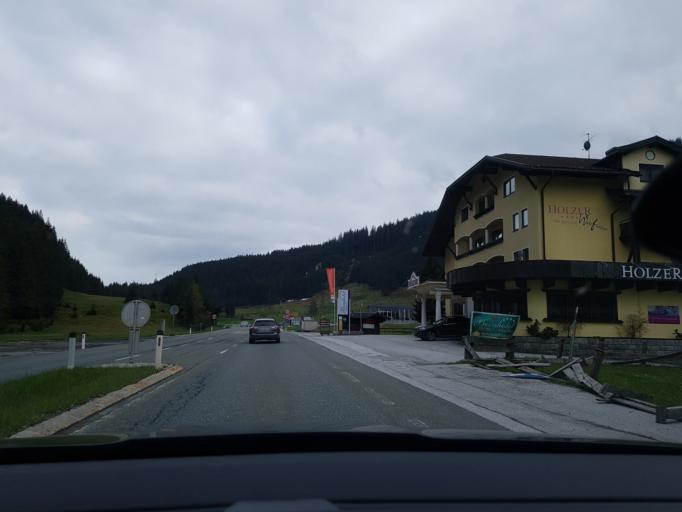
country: AT
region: Salzburg
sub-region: Politischer Bezirk Zell am See
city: Hollersbach im Pinzgau
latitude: 47.3139
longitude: 12.4062
